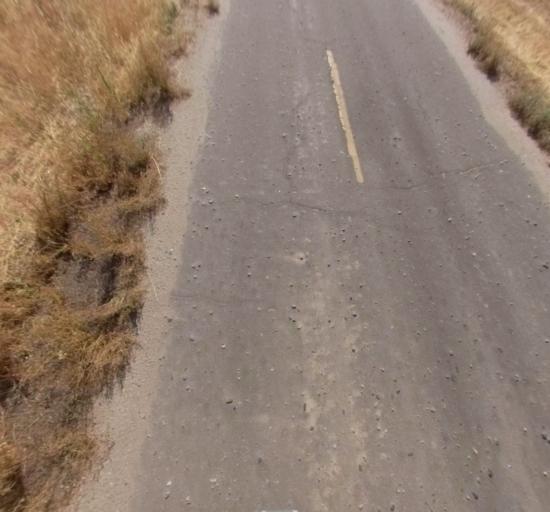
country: US
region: California
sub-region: Madera County
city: Fairmead
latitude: 37.0939
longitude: -120.2180
